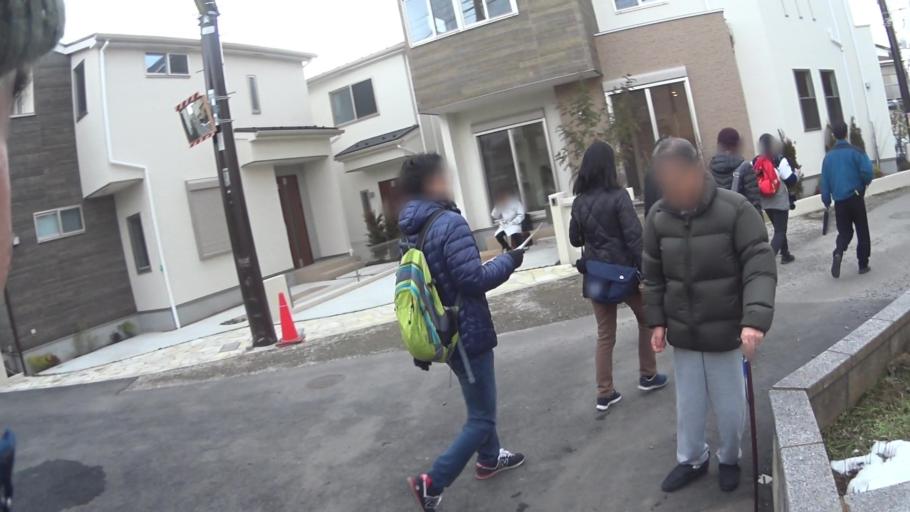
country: JP
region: Saitama
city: Shimotoda
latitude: 35.8538
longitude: 139.6839
